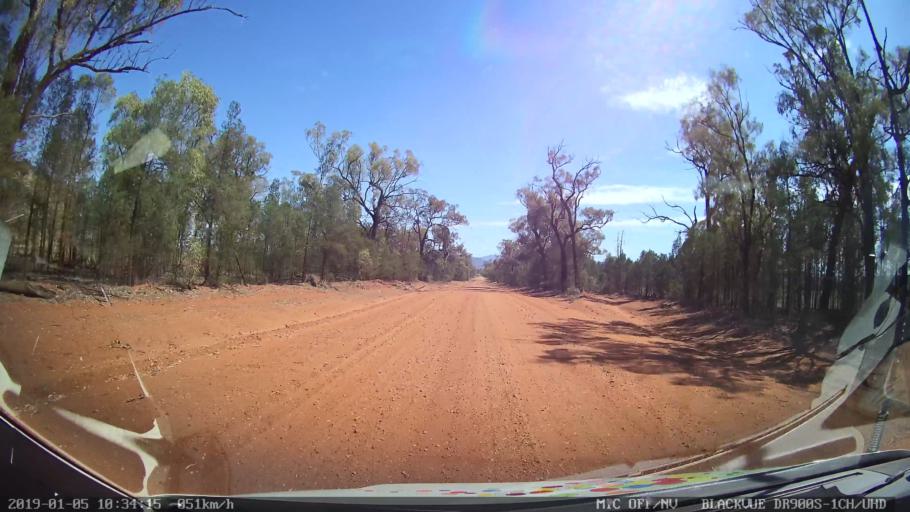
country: AU
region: New South Wales
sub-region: Gilgandra
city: Gilgandra
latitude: -31.4998
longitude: 148.9290
